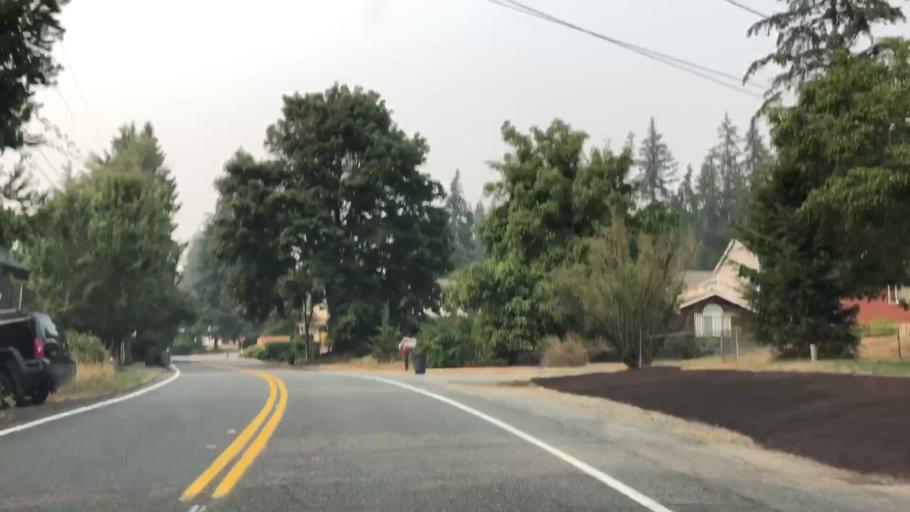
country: US
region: Washington
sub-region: King County
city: Kenmore
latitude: 47.7756
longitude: -122.2407
